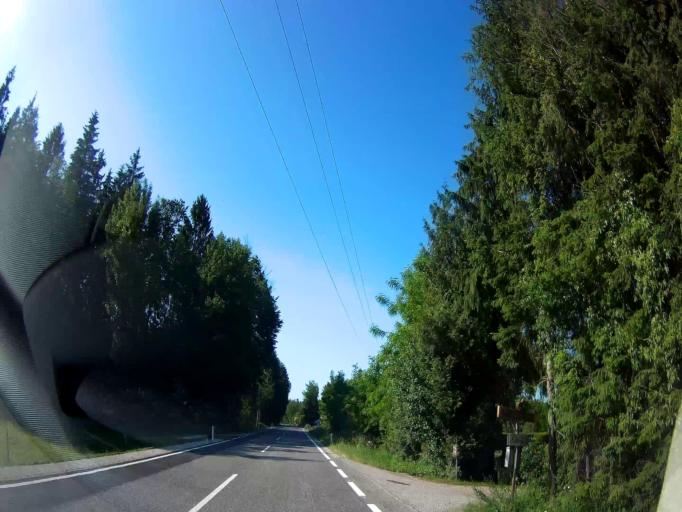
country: AT
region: Upper Austria
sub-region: Politischer Bezirk Braunau am Inn
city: Braunau am Inn
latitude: 48.2077
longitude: 13.0316
